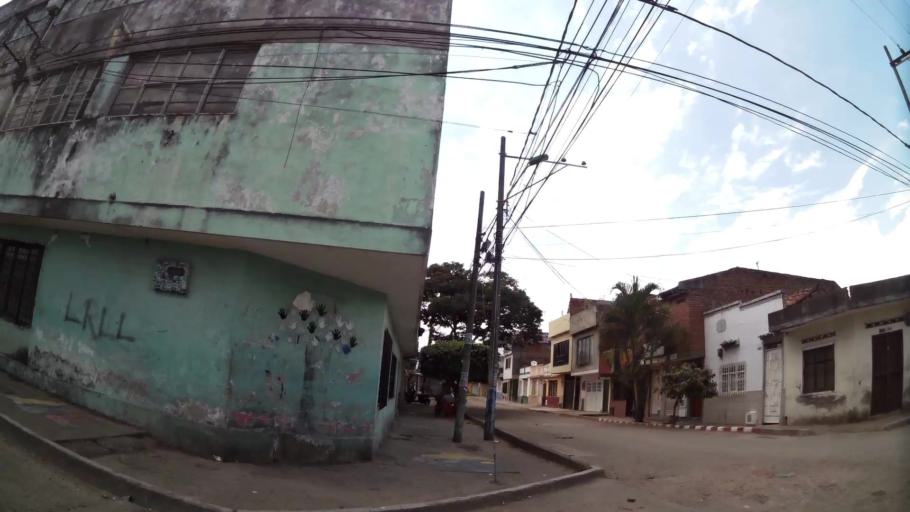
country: CO
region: Valle del Cauca
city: Cali
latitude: 3.4415
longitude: -76.5174
